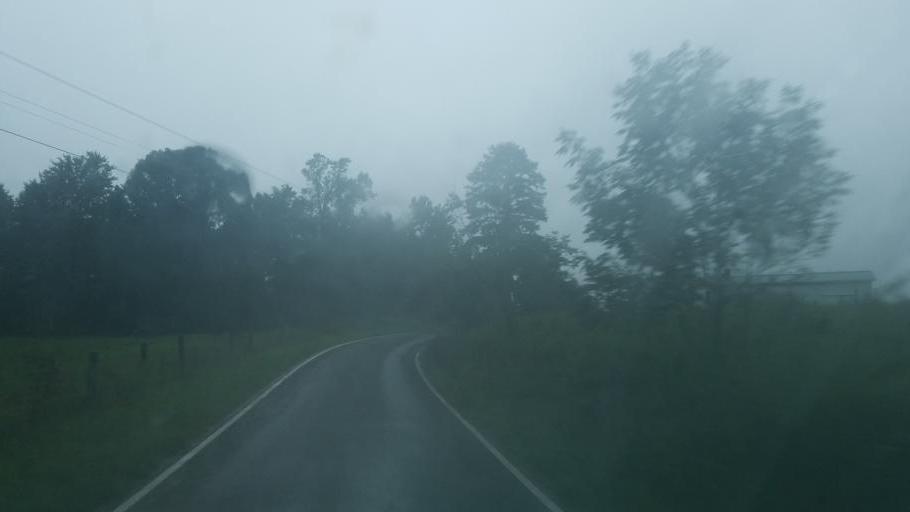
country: US
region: Kentucky
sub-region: Lewis County
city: Vanceburg
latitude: 38.4812
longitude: -83.5107
